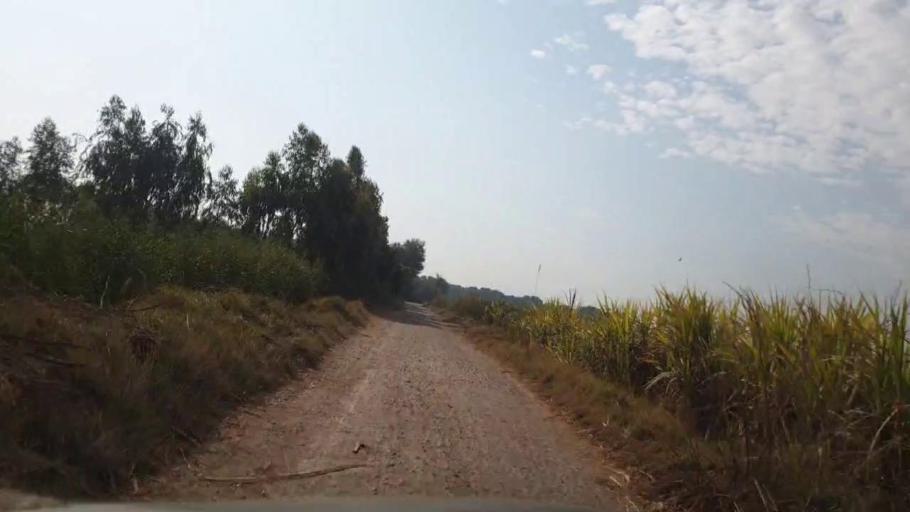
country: PK
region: Sindh
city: Matiari
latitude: 25.5593
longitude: 68.5200
